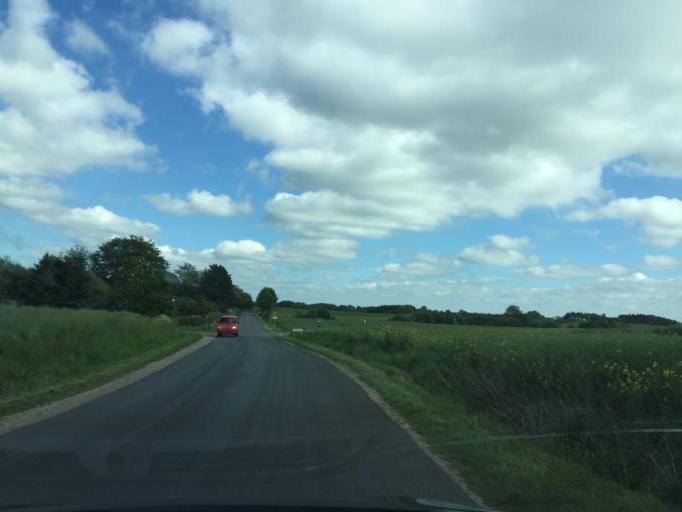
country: DK
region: South Denmark
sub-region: Assens Kommune
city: Tommerup
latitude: 55.3440
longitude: 10.2213
